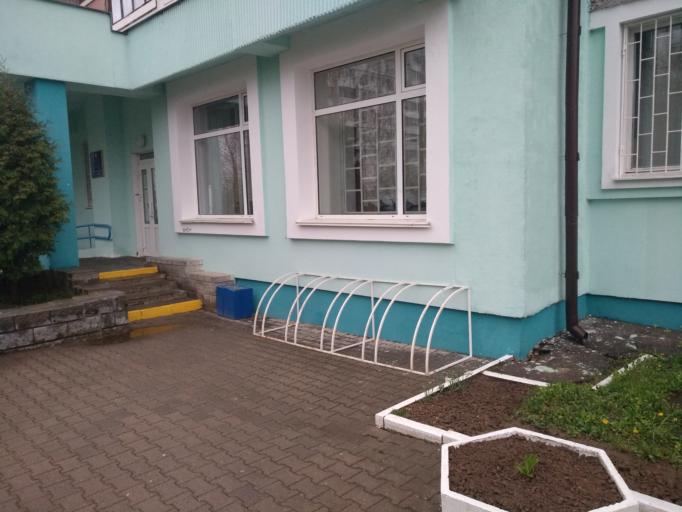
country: BY
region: Minsk
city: Novoye Medvezhino
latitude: 53.8859
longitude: 27.4235
